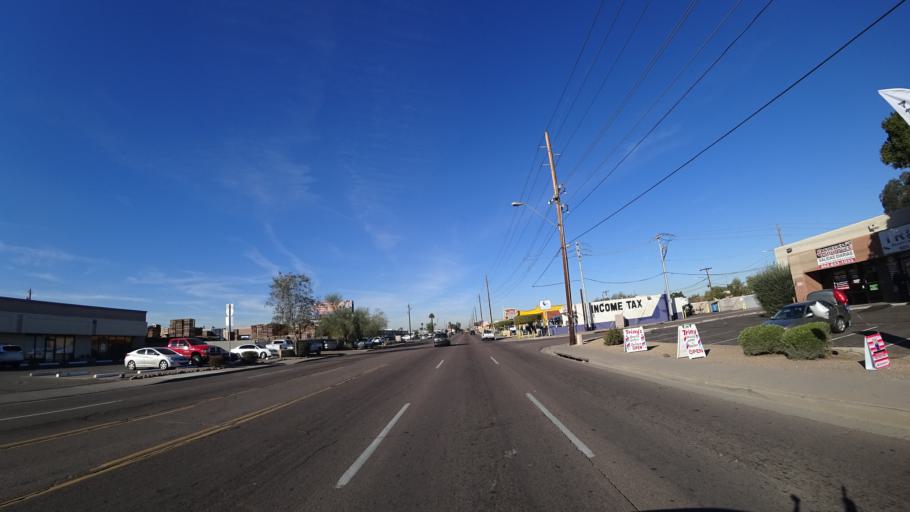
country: US
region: Arizona
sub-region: Maricopa County
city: Phoenix
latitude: 33.4660
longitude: -112.1187
